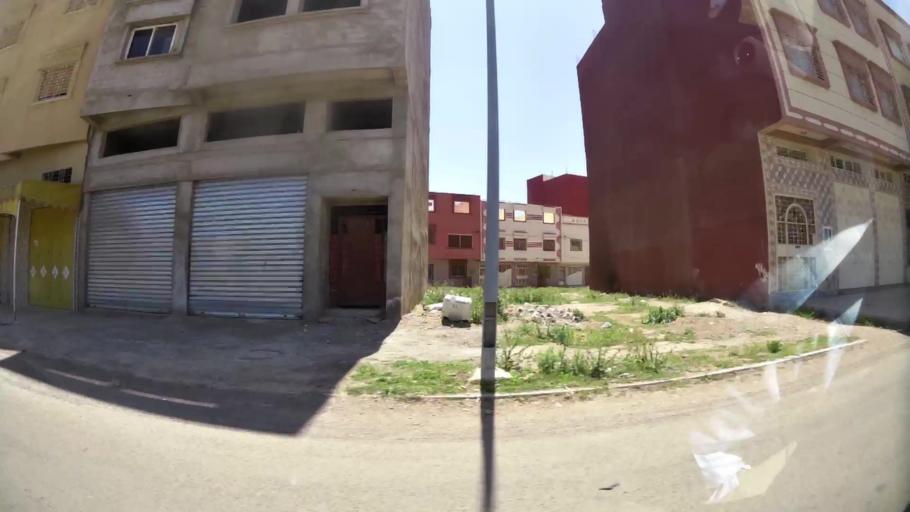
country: MA
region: Oriental
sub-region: Oujda-Angad
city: Oujda
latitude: 34.6646
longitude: -1.9458
